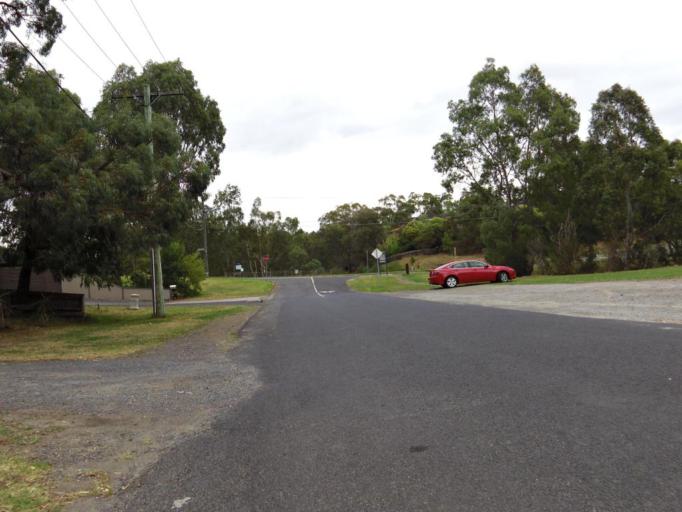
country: AU
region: Victoria
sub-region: Banyule
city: Darch
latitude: -37.7580
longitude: 145.1249
